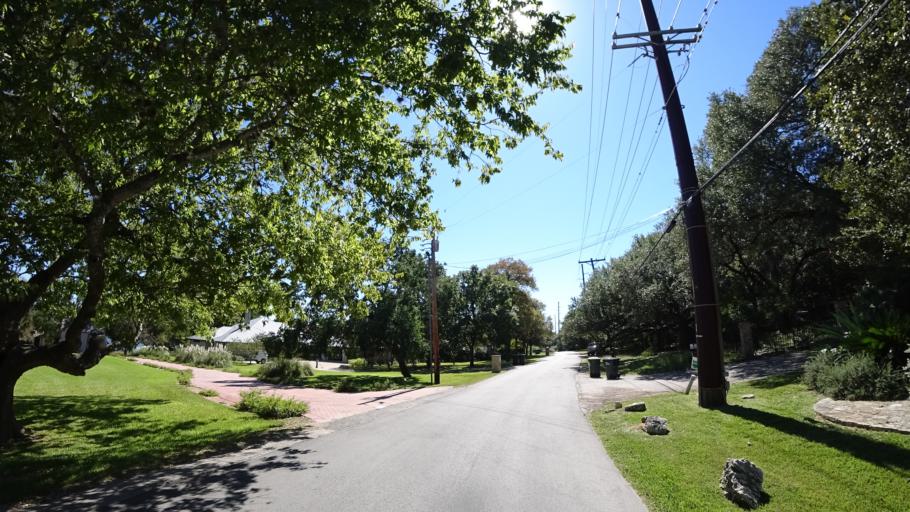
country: US
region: Texas
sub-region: Travis County
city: West Lake Hills
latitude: 30.3092
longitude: -97.7813
